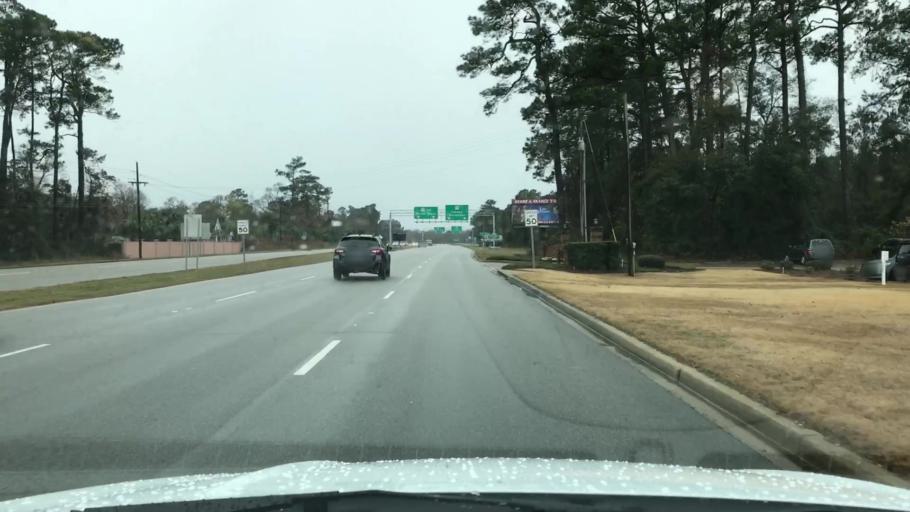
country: US
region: South Carolina
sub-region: Horry County
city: Myrtle Beach
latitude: 33.7747
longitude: -78.7977
